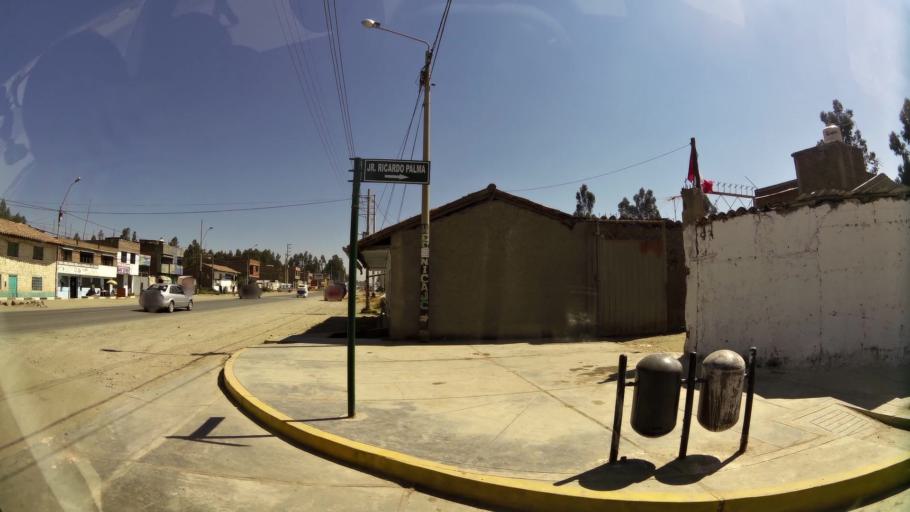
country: PE
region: Junin
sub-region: Provincia de Concepcion
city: Concepcion
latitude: -11.9176
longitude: -75.3225
